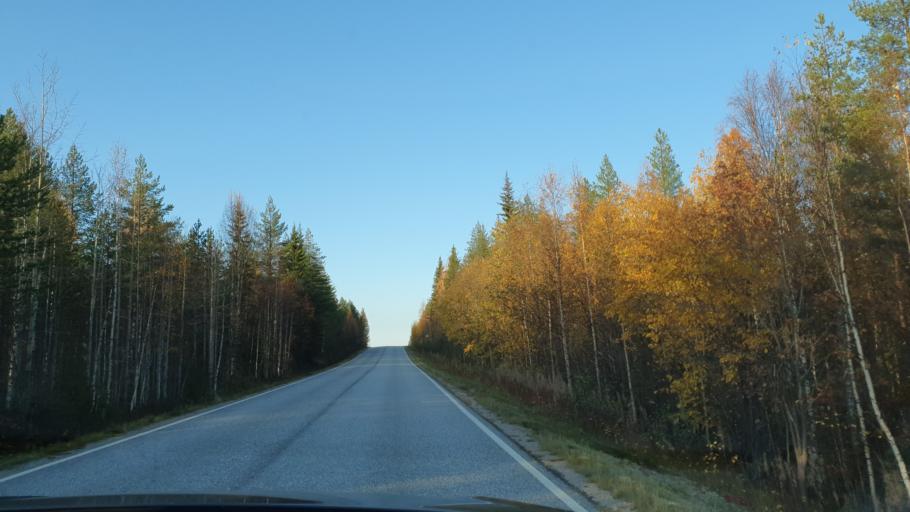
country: FI
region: Kainuu
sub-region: Kehys-Kainuu
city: Kuhmo
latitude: 64.3481
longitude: 29.4883
